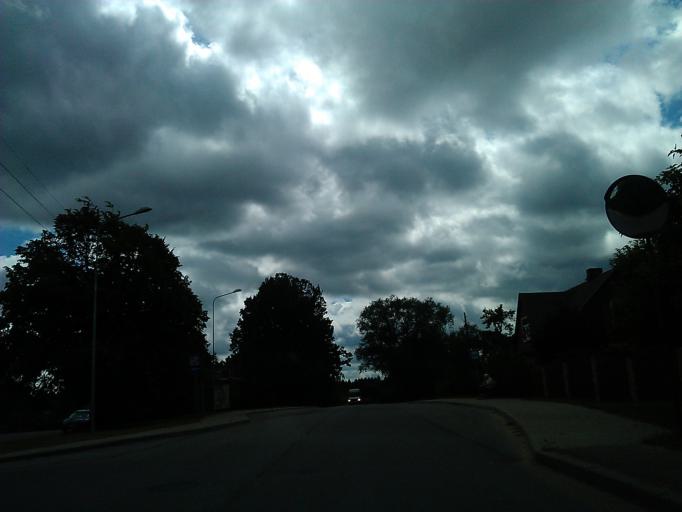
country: LV
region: Kuldigas Rajons
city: Kuldiga
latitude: 56.9633
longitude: 21.9515
